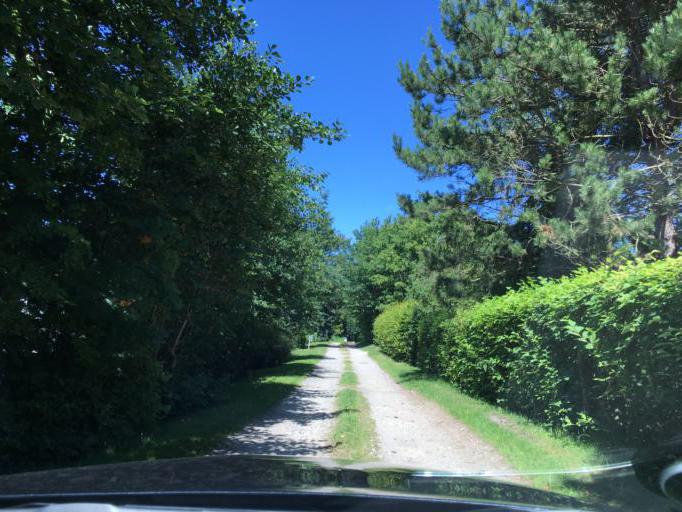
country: DK
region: Capital Region
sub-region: Gribskov Kommune
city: Helsinge
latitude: 56.0942
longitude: 12.1640
